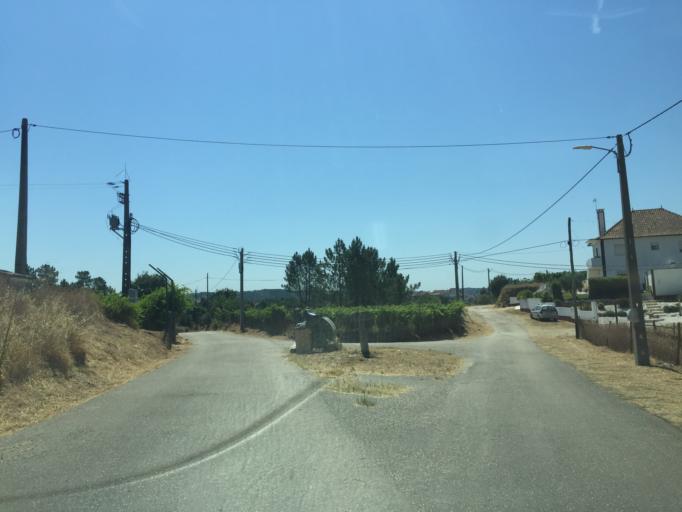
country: PT
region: Santarem
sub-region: Tomar
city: Tomar
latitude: 39.5753
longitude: -8.2996
